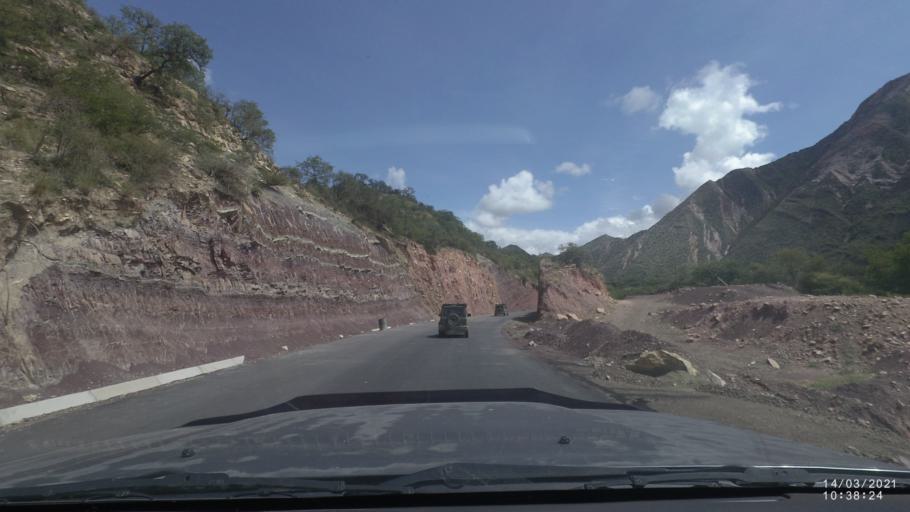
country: BO
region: Cochabamba
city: Cliza
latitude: -17.8941
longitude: -65.8926
